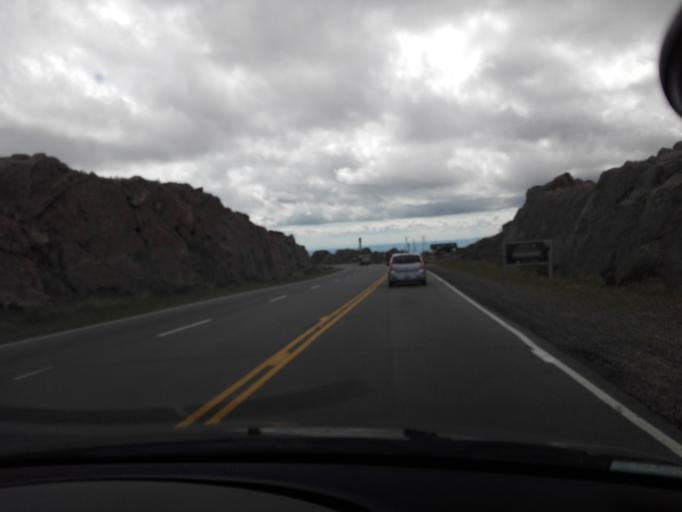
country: AR
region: Cordoba
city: Villa Cura Brochero
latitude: -31.6128
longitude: -64.9049
